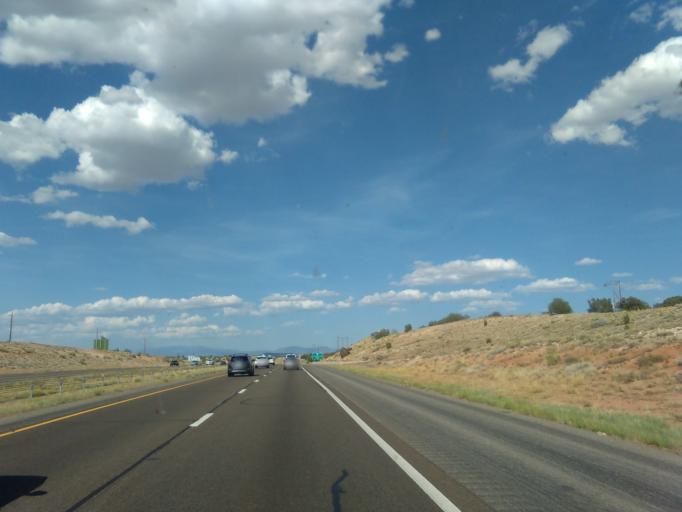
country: US
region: New Mexico
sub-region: Sandoval County
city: Santo Domingo Pueblo
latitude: 35.4602
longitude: -106.3288
